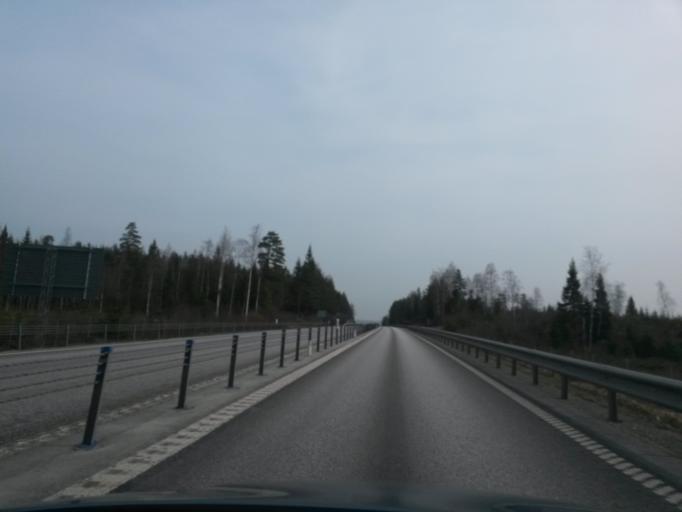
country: SE
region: Vaestra Goetaland
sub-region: Gullspangs Kommun
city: Anderstorp
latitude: 58.9103
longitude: 14.3686
